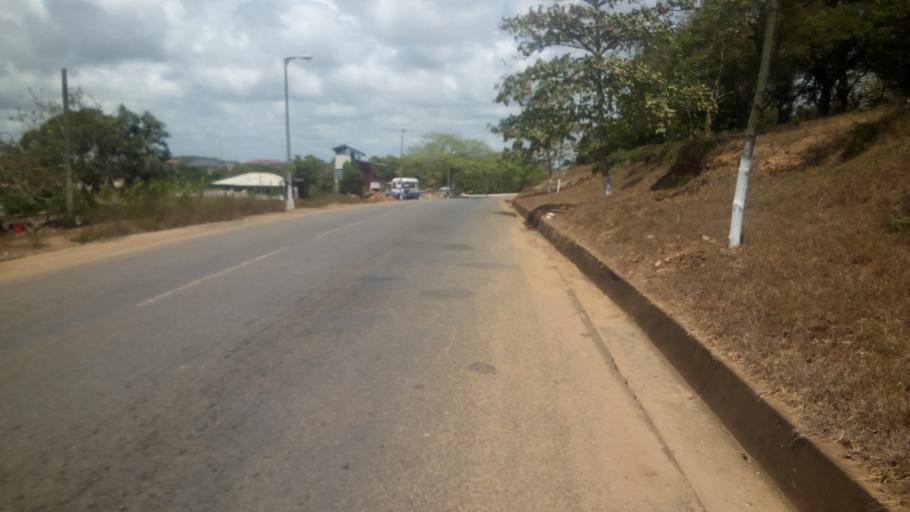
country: GH
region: Central
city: Cape Coast
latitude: 5.1096
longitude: -1.2867
